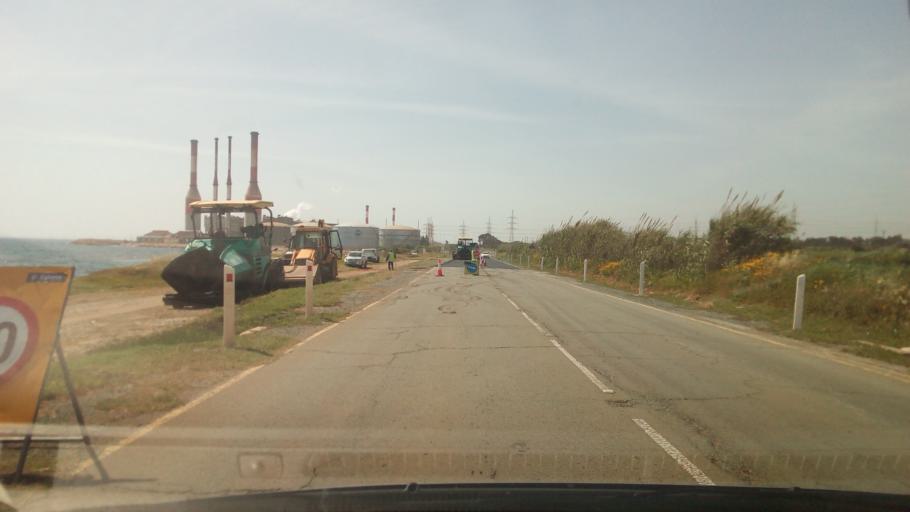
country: CY
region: Larnaka
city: Xylotymbou
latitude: 34.9824
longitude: 33.7541
